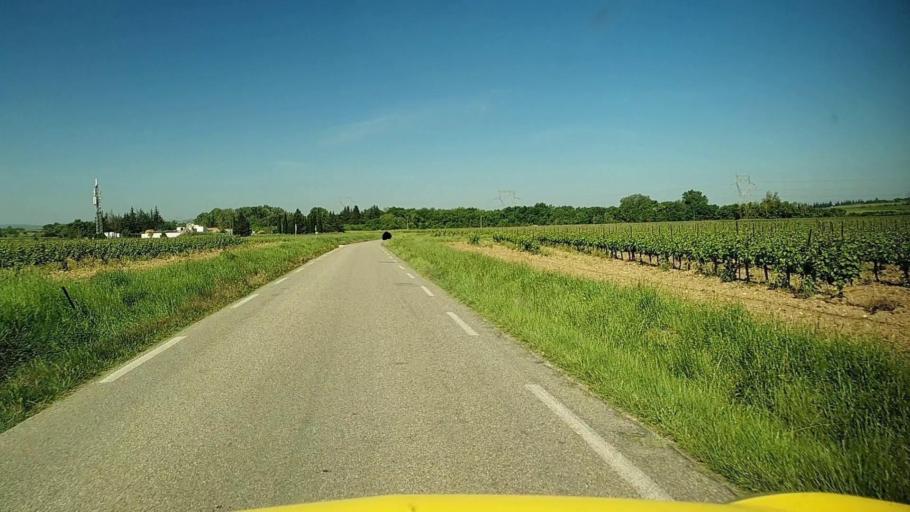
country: FR
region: Languedoc-Roussillon
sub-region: Departement du Gard
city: Saint-Chaptes
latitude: 43.9422
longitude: 4.3199
